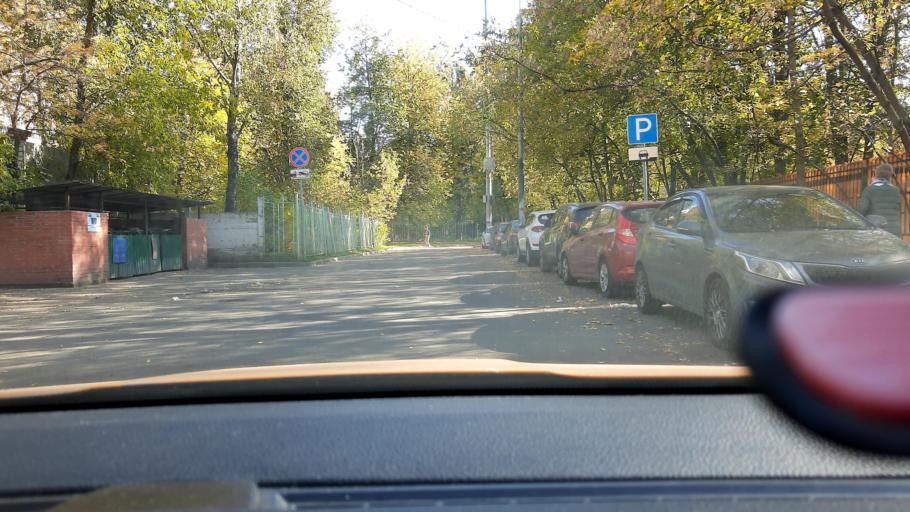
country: RU
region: Moskovskaya
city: Levoberezhnyy
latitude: 55.8406
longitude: 37.4583
